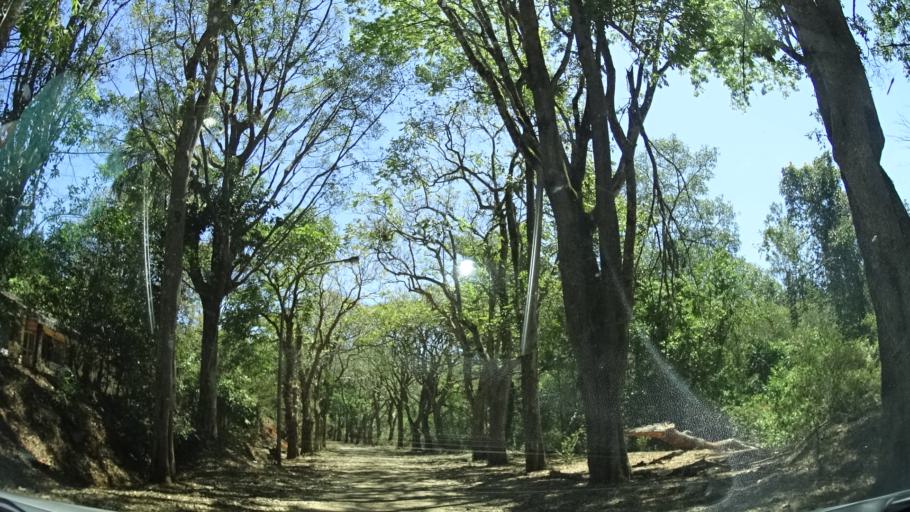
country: IN
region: Karnataka
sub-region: Chikmagalur
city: Sringeri
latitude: 13.2224
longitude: 75.2553
